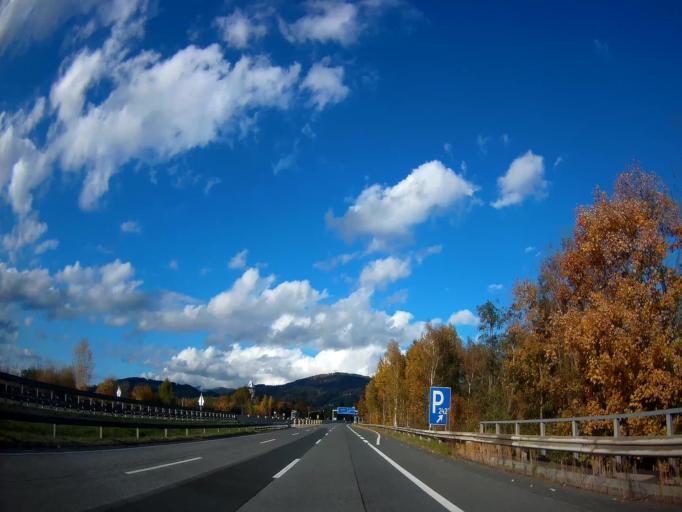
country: AT
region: Carinthia
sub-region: Politischer Bezirk Wolfsberg
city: Bad Sankt Leonhard im Lavanttal
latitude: 46.9255
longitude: 14.8415
